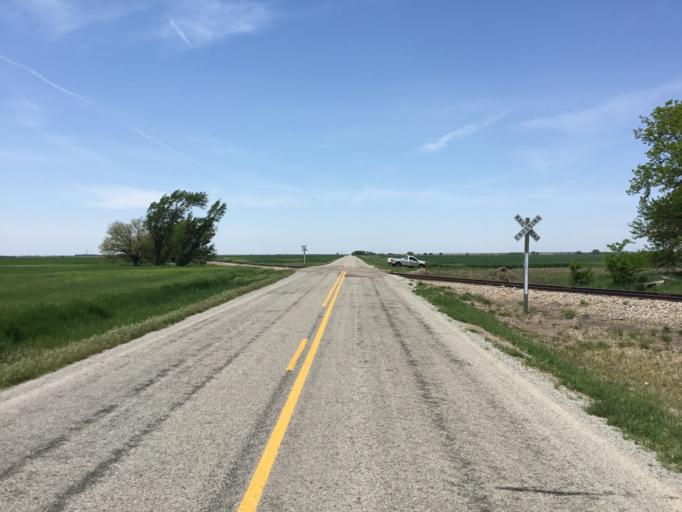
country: US
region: Kansas
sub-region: Mitchell County
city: Beloit
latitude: 39.5388
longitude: -97.9748
